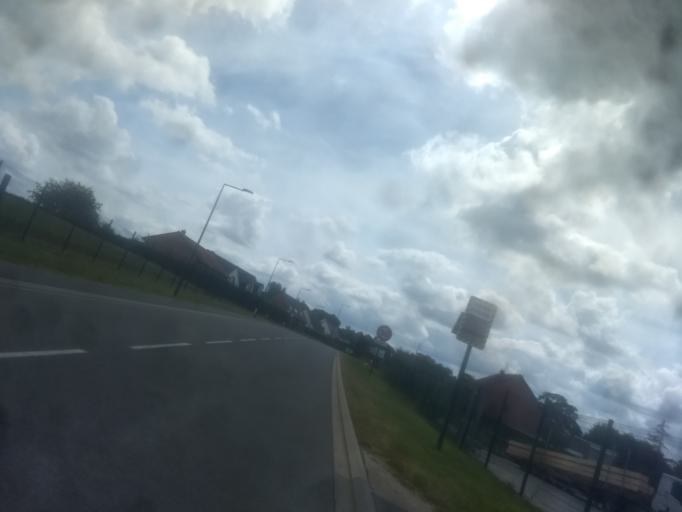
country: FR
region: Nord-Pas-de-Calais
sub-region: Departement du Pas-de-Calais
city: Duisans
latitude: 50.3346
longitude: 2.6432
